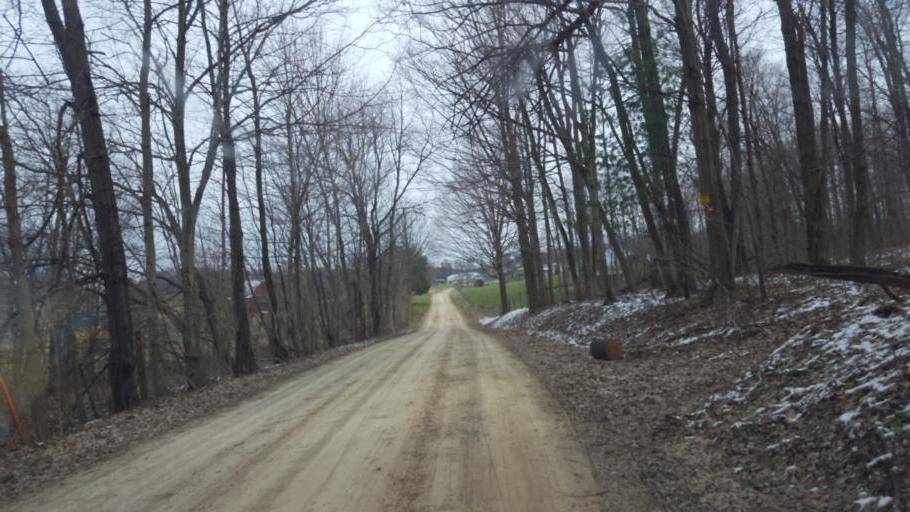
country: US
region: Ohio
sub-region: Knox County
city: Danville
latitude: 40.5230
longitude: -82.3646
